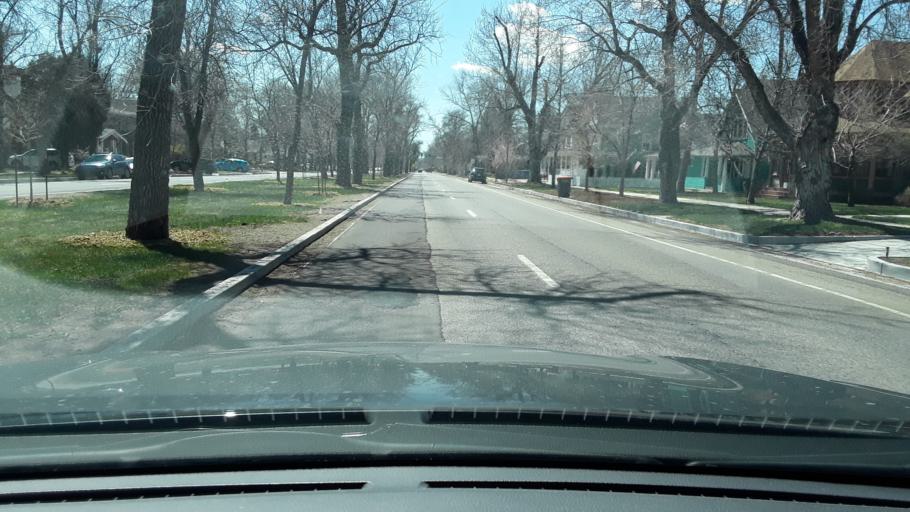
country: US
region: Colorado
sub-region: El Paso County
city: Colorado Springs
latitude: 38.8629
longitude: -104.8203
